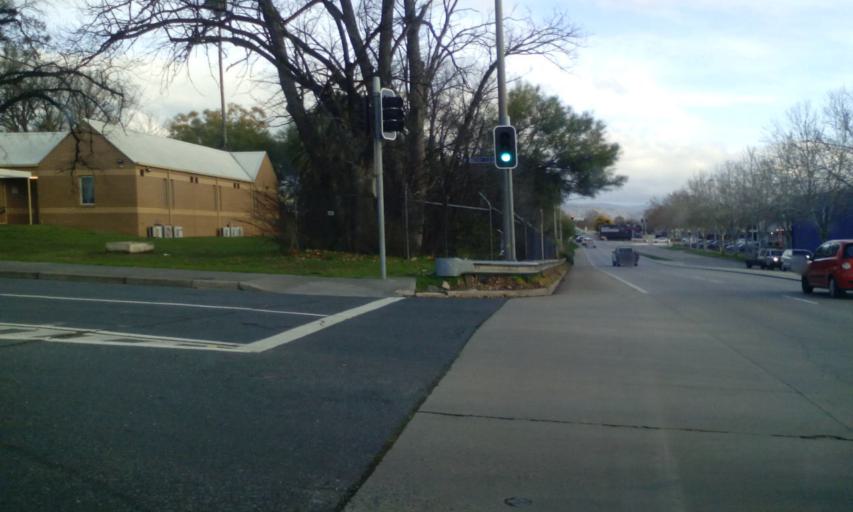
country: AU
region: New South Wales
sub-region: Albury Municipality
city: East Albury
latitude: -36.0837
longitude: 146.9234
